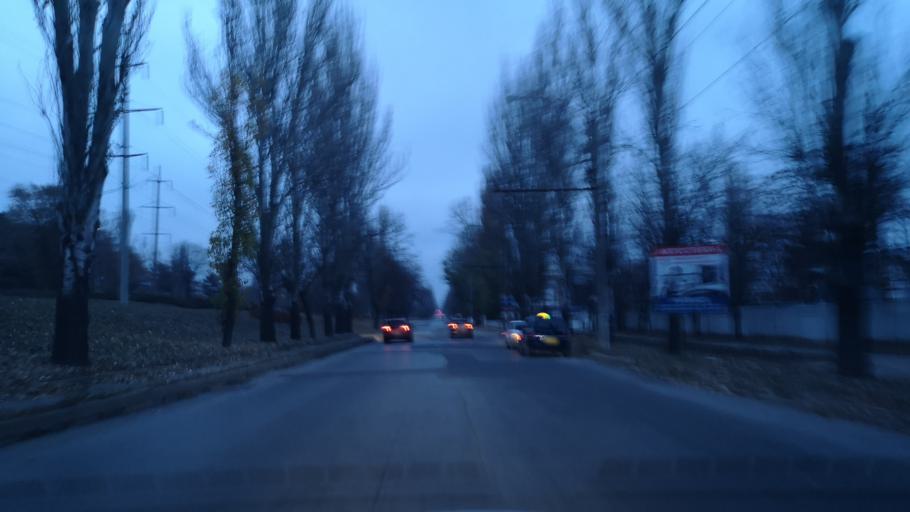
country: MD
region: Chisinau
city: Chisinau
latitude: 47.0144
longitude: 28.8876
